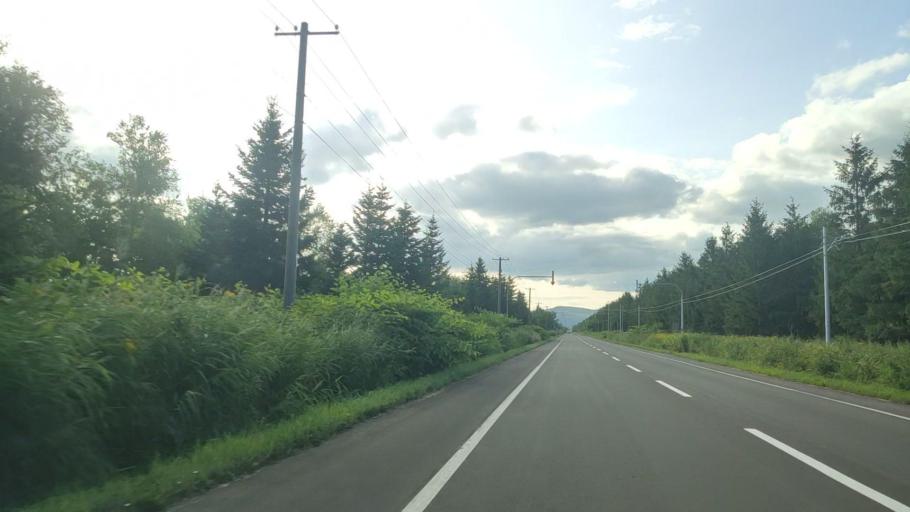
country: JP
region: Hokkaido
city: Makubetsu
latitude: 44.8841
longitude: 142.0139
